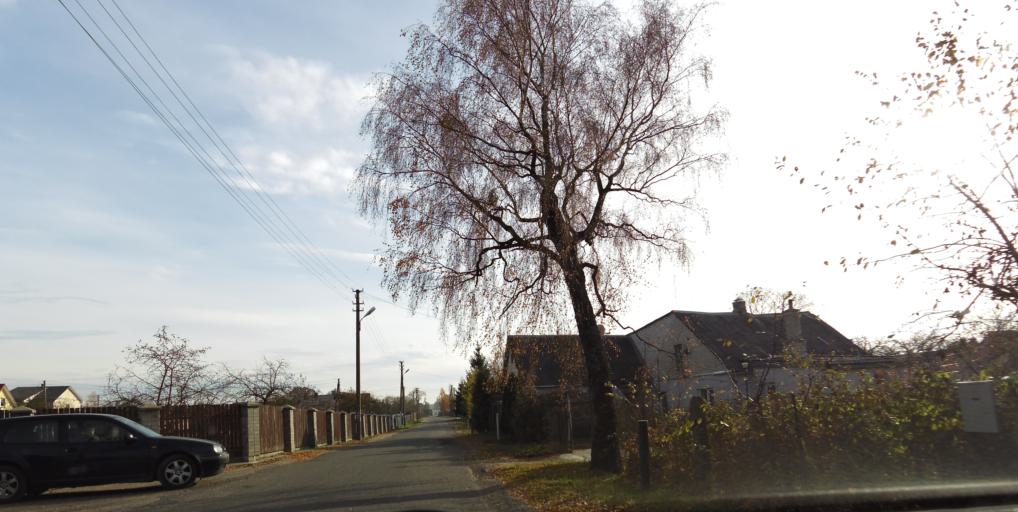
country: LT
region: Vilnius County
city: Pilaite
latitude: 54.7281
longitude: 25.1786
